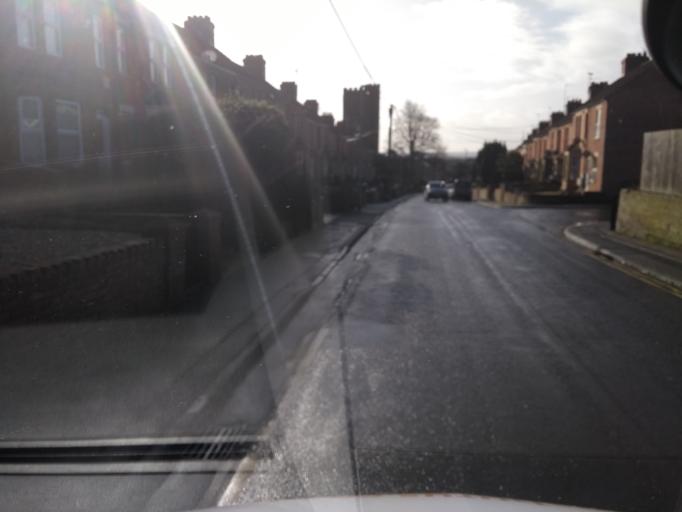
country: GB
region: England
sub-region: Somerset
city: Yeovil
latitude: 50.9486
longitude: -2.6212
